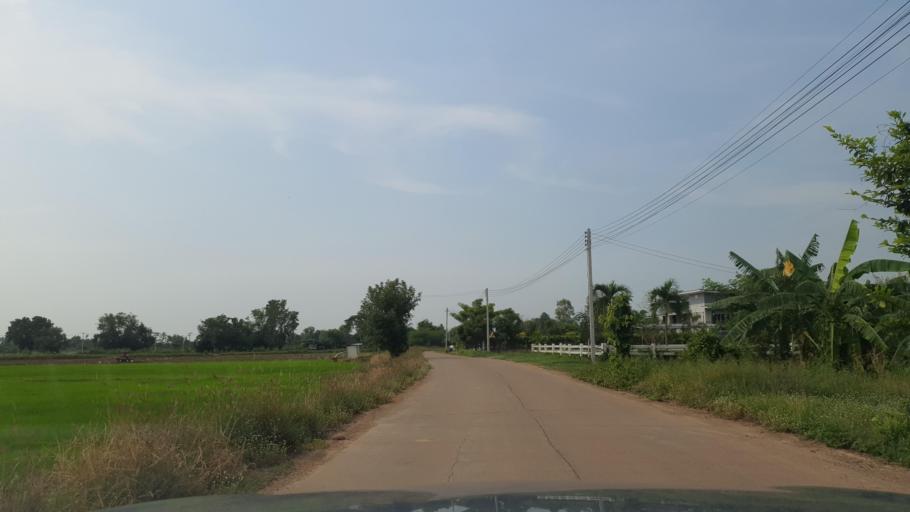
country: TH
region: Phitsanulok
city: Bang Rakam
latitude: 16.7987
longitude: 100.1634
